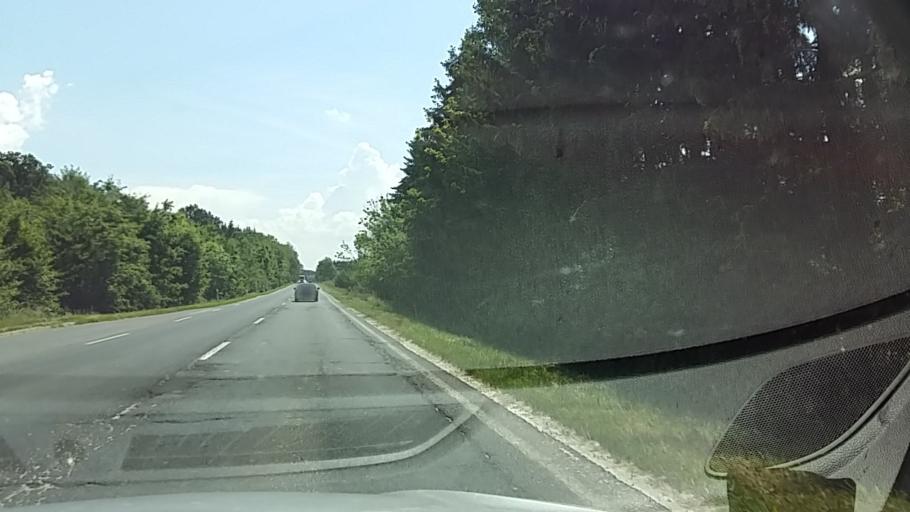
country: AT
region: Burgenland
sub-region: Politischer Bezirk Gussing
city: Inzenhof
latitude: 46.9804
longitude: 16.3136
